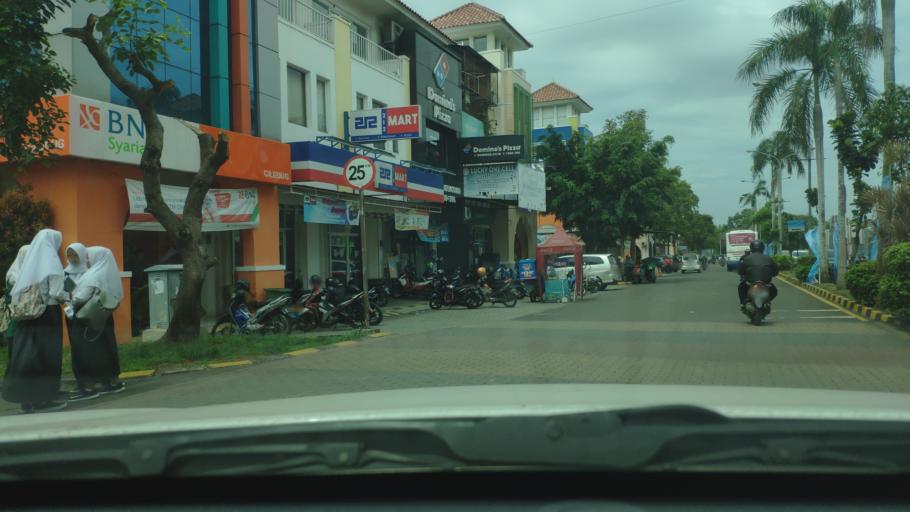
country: ID
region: West Java
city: Ciputat
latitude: -6.2229
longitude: 106.7092
